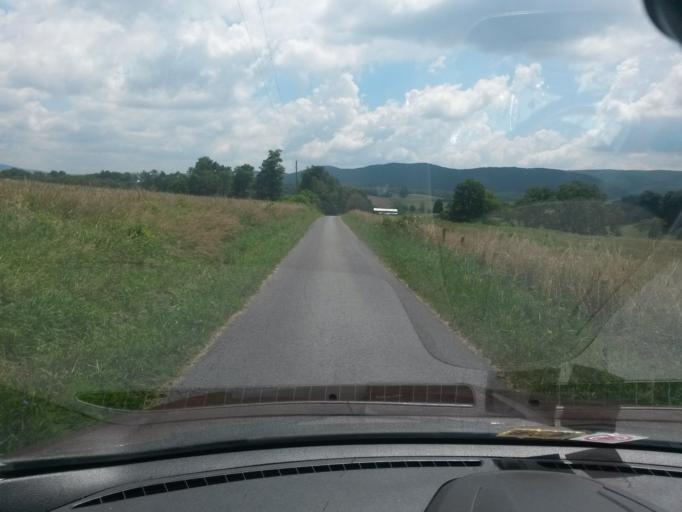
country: US
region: West Virginia
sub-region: Monroe County
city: Union
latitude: 37.5647
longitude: -80.4973
